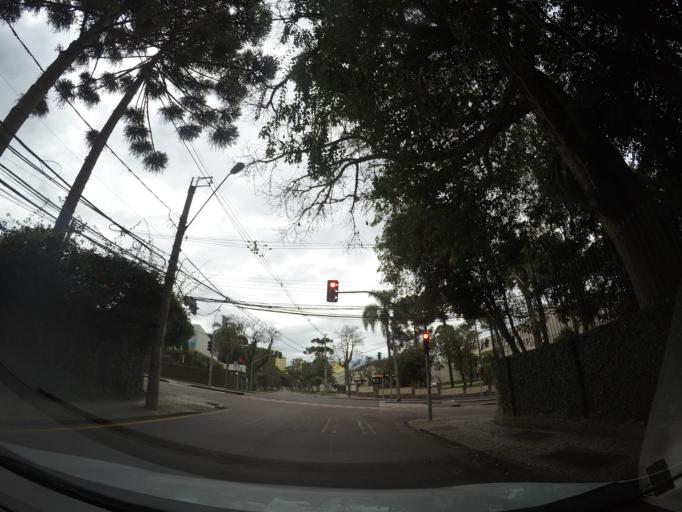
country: BR
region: Parana
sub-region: Curitiba
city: Curitiba
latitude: -25.4224
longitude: -49.2670
